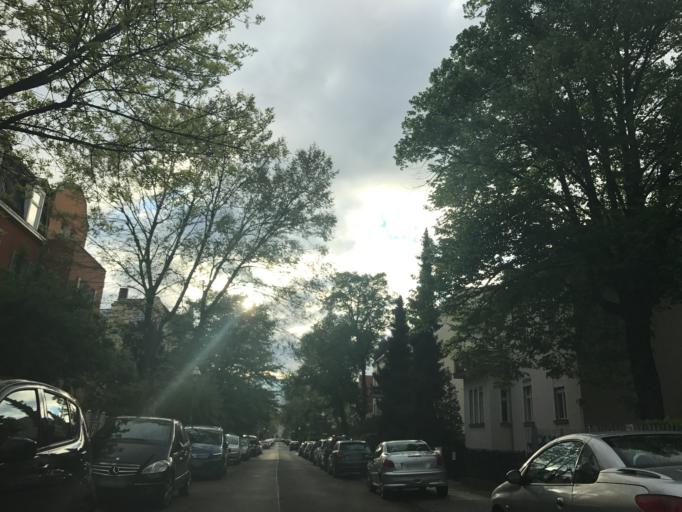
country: DE
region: Berlin
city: Westend
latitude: 52.5156
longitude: 13.2691
